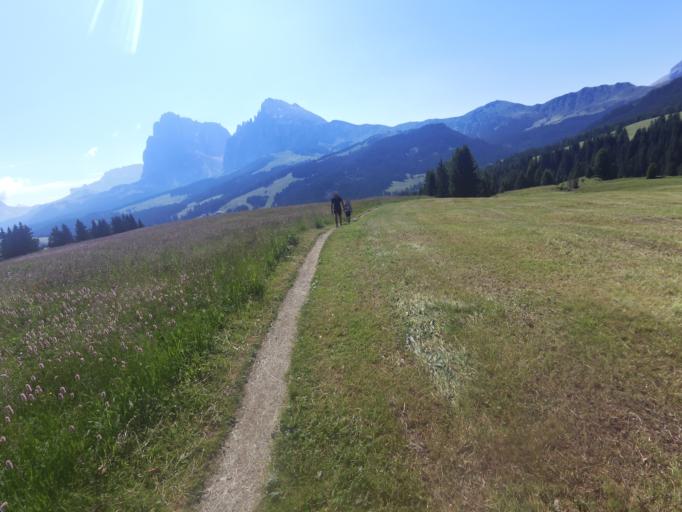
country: IT
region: Trentino-Alto Adige
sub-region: Bolzano
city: Ortisei
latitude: 46.5346
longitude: 11.6553
